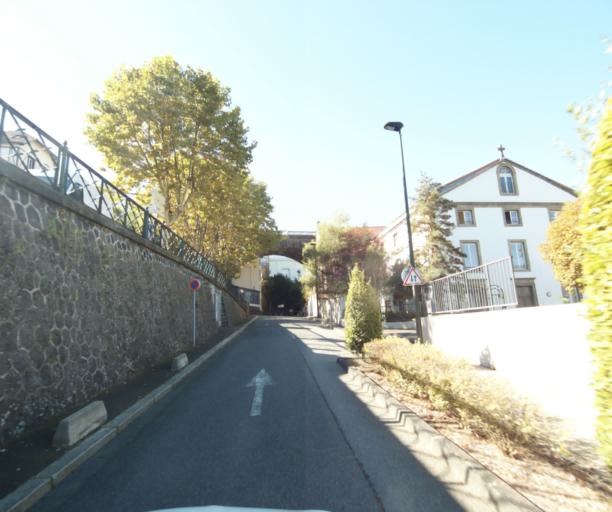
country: FR
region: Auvergne
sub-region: Departement du Puy-de-Dome
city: Chamalieres
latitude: 45.7694
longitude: 3.0598
